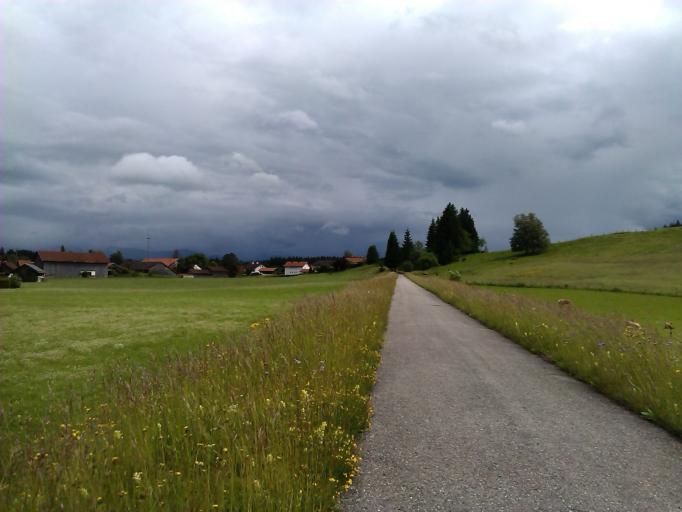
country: DE
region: Bavaria
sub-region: Swabia
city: Stotten am Auerberg
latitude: 47.7085
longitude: 10.6953
